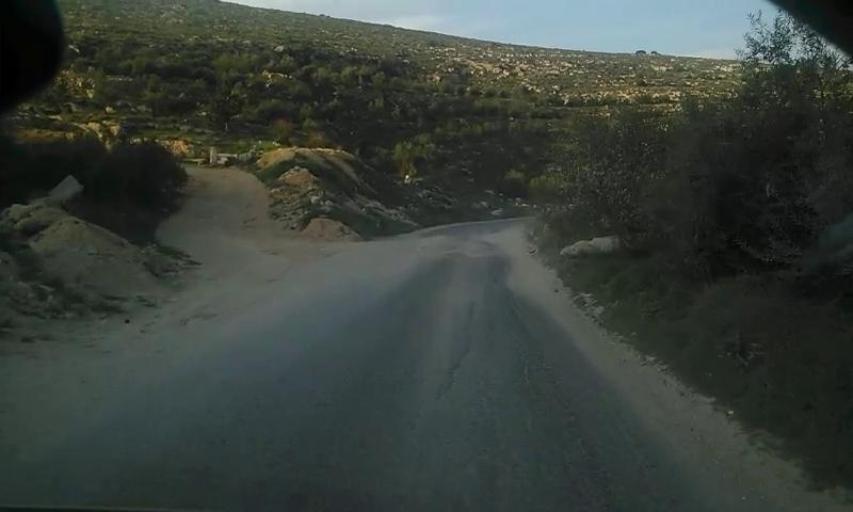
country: PS
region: West Bank
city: Marah Rabbah
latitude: 31.5991
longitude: 35.1812
